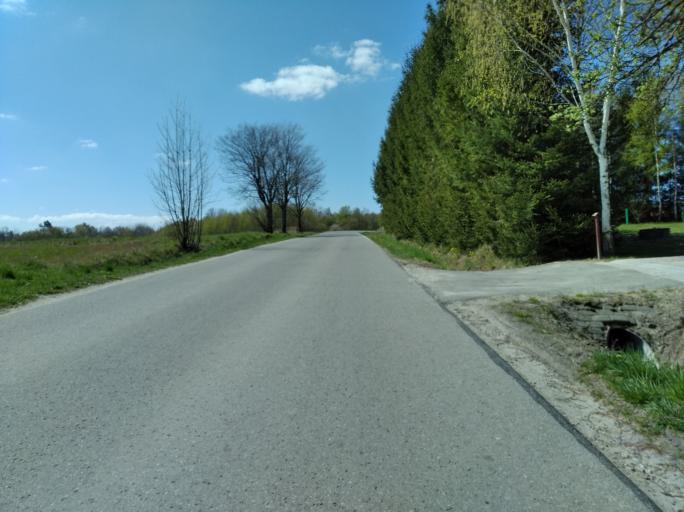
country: PL
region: Subcarpathian Voivodeship
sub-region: Powiat strzyzowski
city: Wisniowa
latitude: 49.9042
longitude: 21.6726
